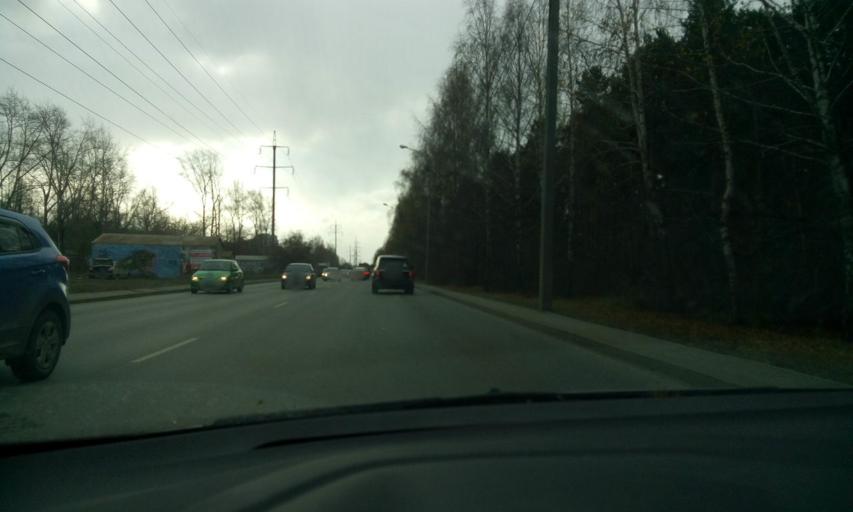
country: RU
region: Sverdlovsk
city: Sovkhoznyy
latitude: 56.7830
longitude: 60.5981
